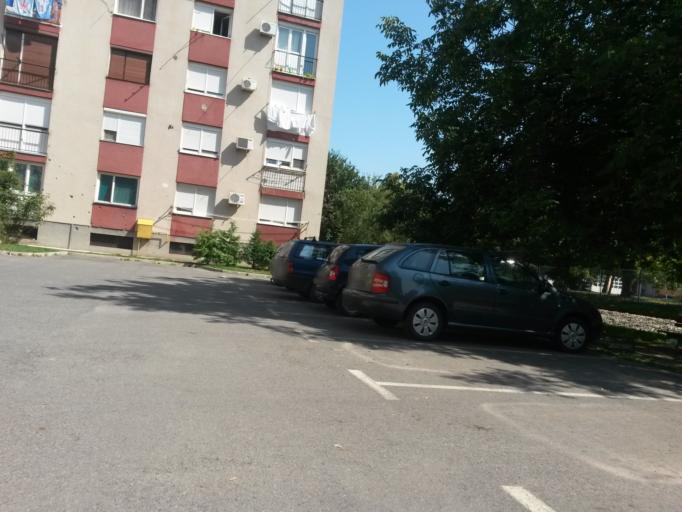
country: HR
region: Osjecko-Baranjska
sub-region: Grad Osijek
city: Osijek
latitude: 45.5542
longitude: 18.7030
